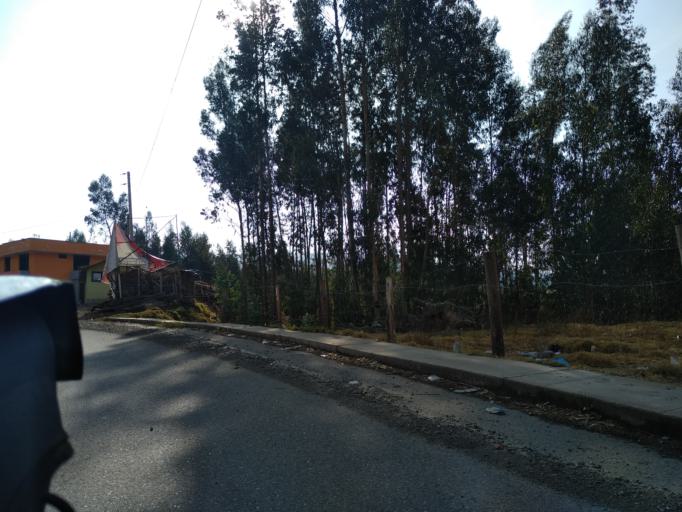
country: PE
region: La Libertad
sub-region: Provincia de Otuzco
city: Agallpampa
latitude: -7.9944
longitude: -78.5163
